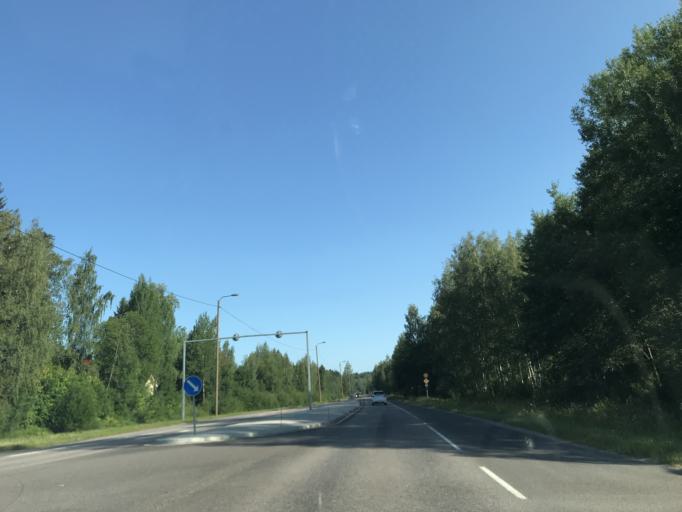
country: FI
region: Paijanne Tavastia
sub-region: Lahti
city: Lahti
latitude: 61.0213
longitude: 25.6777
